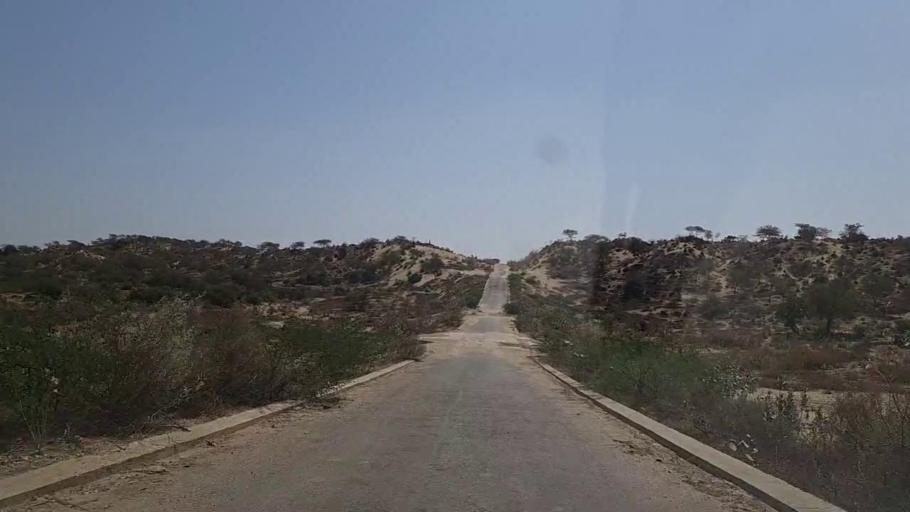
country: PK
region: Sindh
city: Diplo
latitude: 24.5079
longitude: 69.4234
